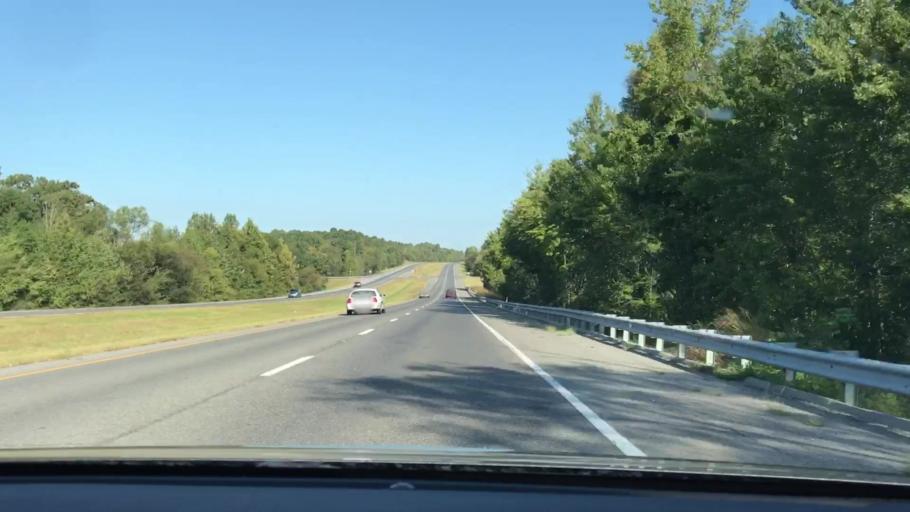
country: US
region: Kentucky
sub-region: Marshall County
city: Benton
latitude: 36.7724
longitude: -88.3165
